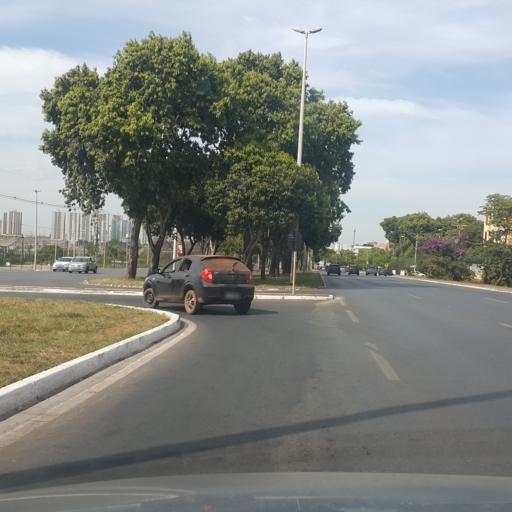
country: BR
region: Federal District
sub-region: Brasilia
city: Brasilia
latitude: -15.8171
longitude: -48.0579
